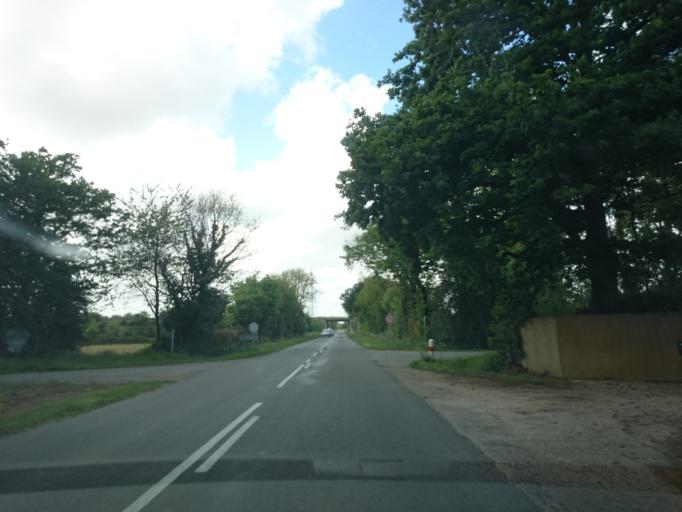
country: FR
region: Pays de la Loire
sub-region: Departement de la Loire-Atlantique
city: La Montagne
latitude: 47.1685
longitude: -1.6744
